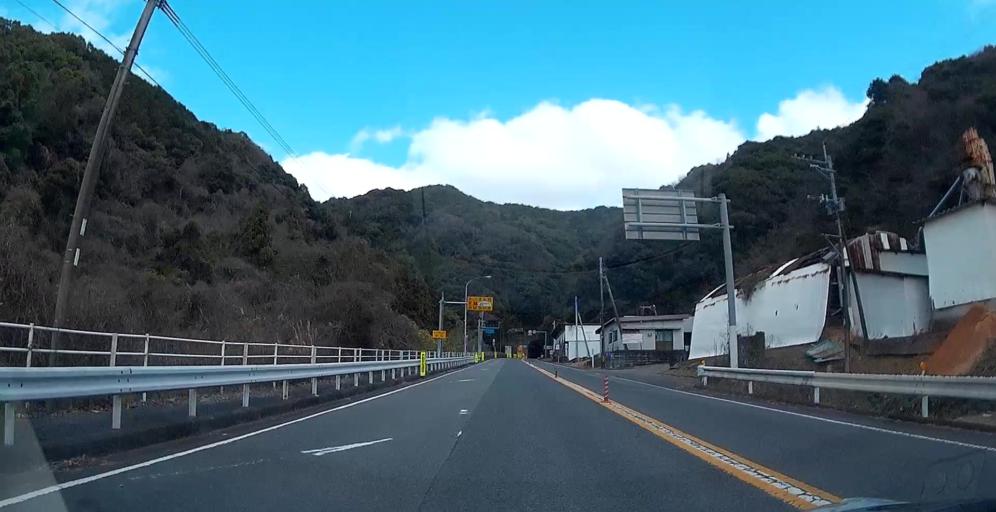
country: JP
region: Kumamoto
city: Yatsushiro
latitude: 32.3696
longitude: 130.5266
